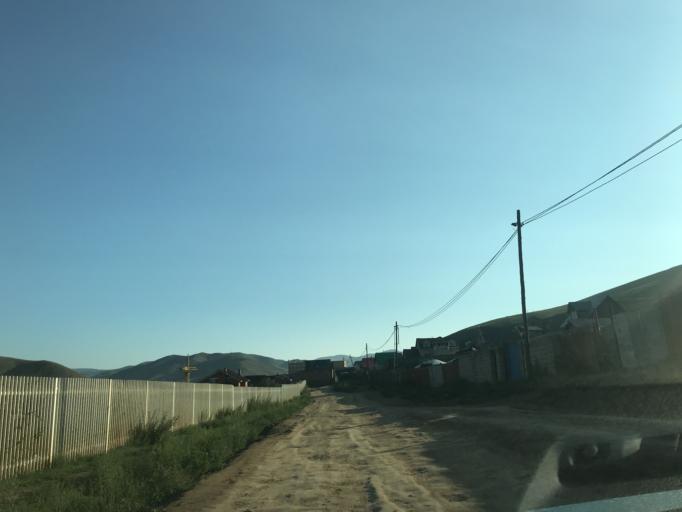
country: MN
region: Ulaanbaatar
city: Ulaanbaatar
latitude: 47.9932
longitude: 106.9679
